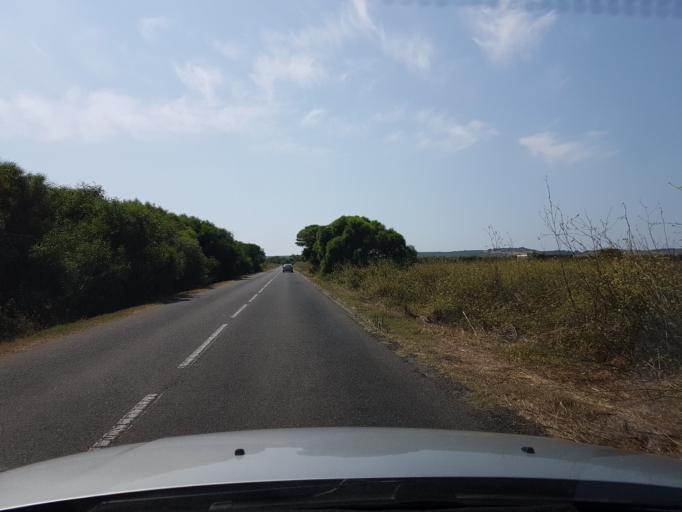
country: IT
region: Sardinia
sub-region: Provincia di Oristano
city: Cabras
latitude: 39.9164
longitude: 8.4791
